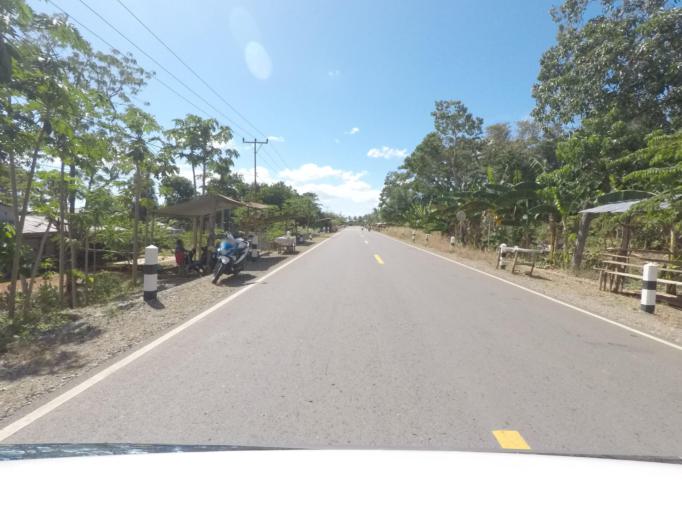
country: TL
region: Baucau
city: Baucau
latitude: -8.4908
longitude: 126.3654
